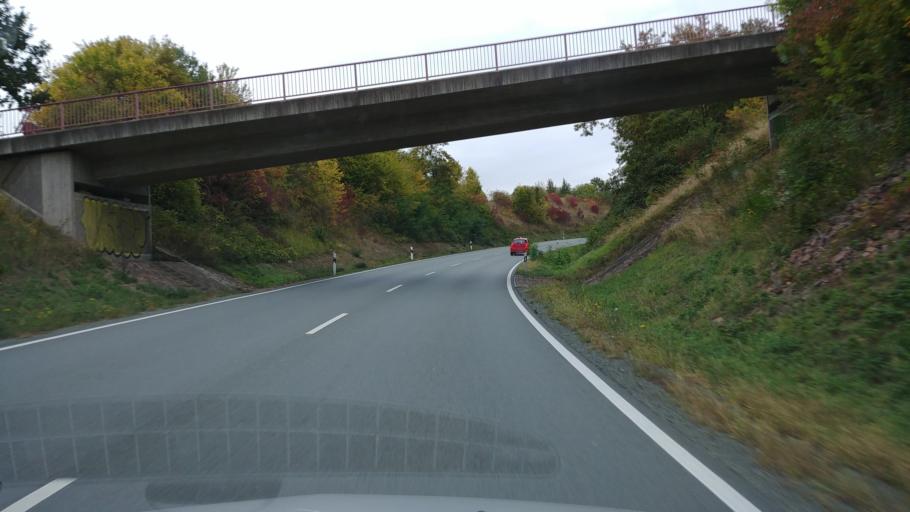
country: DE
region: Hesse
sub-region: Regierungsbezirk Giessen
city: Limburg an der Lahn
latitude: 50.3670
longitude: 8.0336
